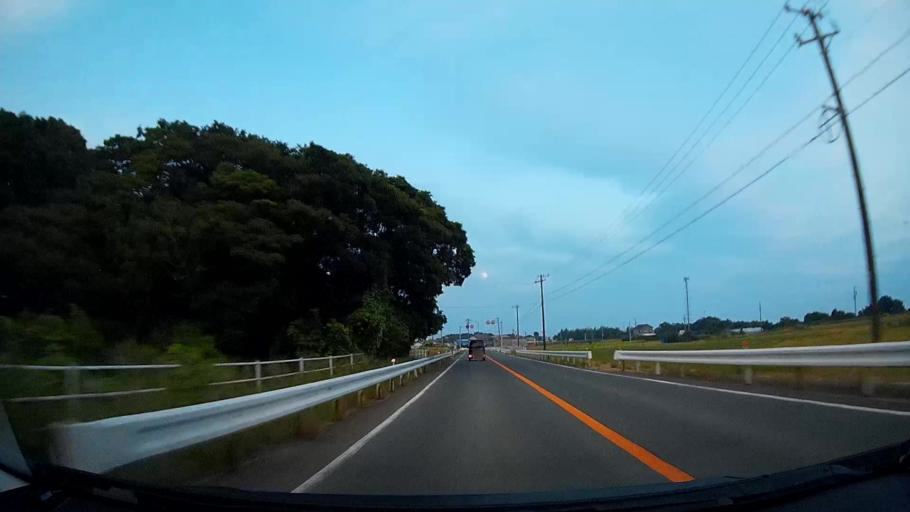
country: JP
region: Shizuoka
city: Kosai-shi
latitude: 34.6853
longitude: 137.5007
